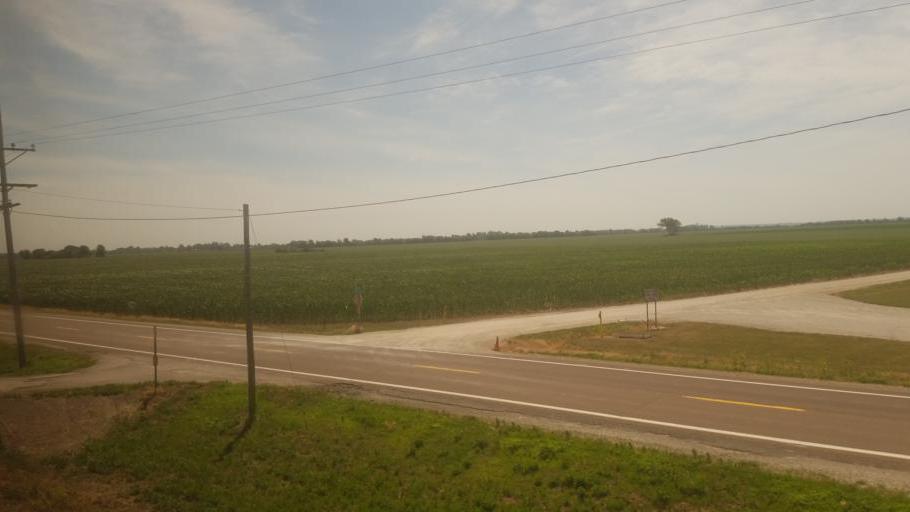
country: US
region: Missouri
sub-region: Carroll County
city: Carrollton
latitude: 39.3176
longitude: -93.6108
